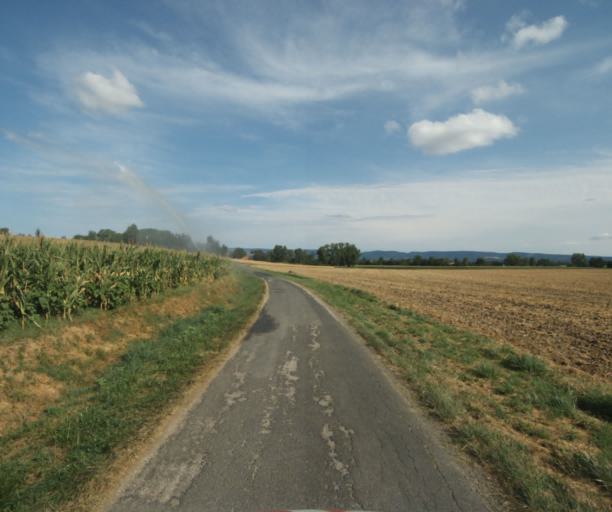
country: FR
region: Midi-Pyrenees
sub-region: Departement du Tarn
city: Puylaurens
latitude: 43.5227
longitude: 1.9794
